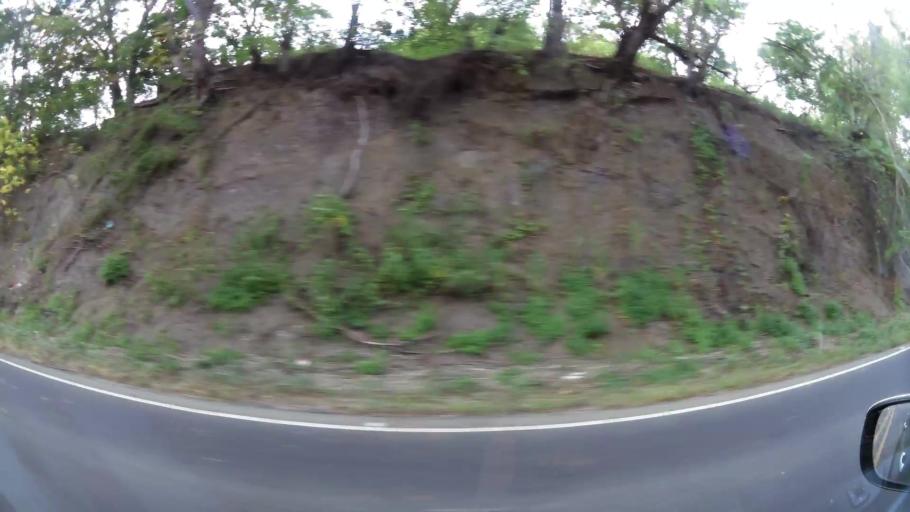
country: CR
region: Guanacaste
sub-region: Canton de Nicoya
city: Nicoya
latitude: 10.1576
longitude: -85.3068
